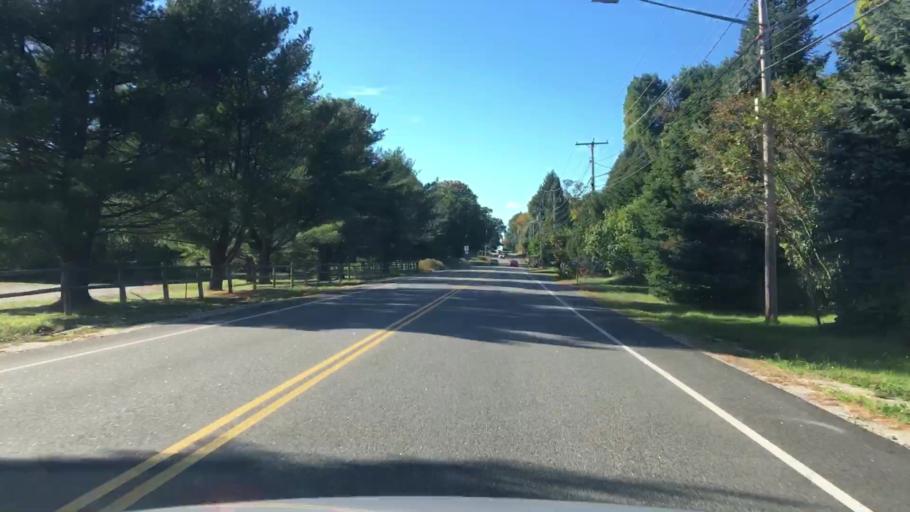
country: US
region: Maine
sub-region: Androscoggin County
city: Lewiston
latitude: 44.0807
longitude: -70.1676
